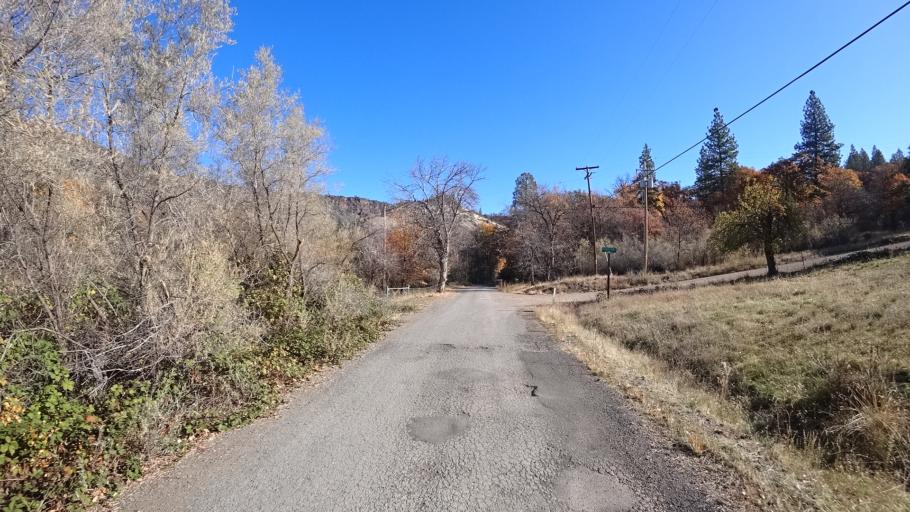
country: US
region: California
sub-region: Siskiyou County
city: Montague
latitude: 41.9642
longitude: -122.2595
